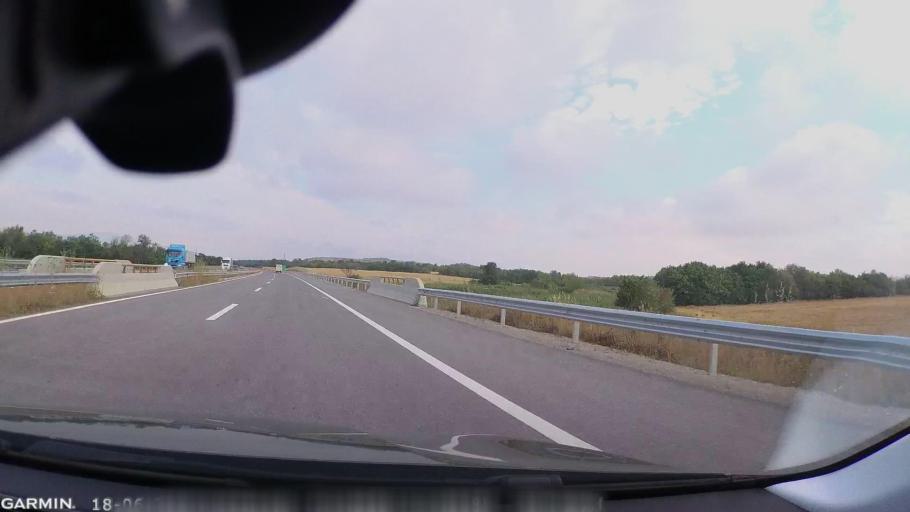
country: MK
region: Sveti Nikole
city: Sveti Nikole
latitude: 41.8410
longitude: 21.9814
